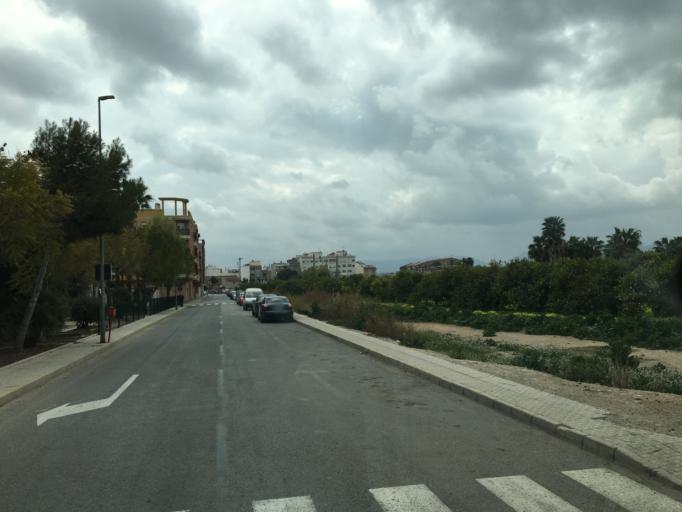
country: ES
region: Murcia
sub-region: Murcia
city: Beniel
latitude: 38.0469
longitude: -1.0052
